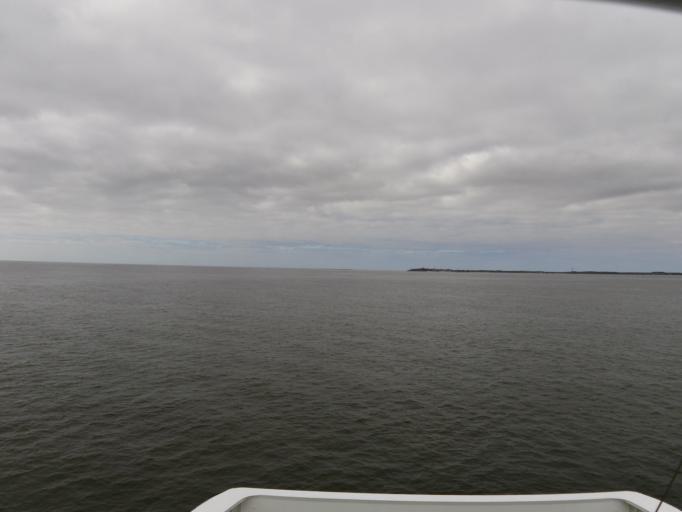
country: DE
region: Schleswig-Holstein
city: Witsum
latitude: 54.6411
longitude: 8.4479
